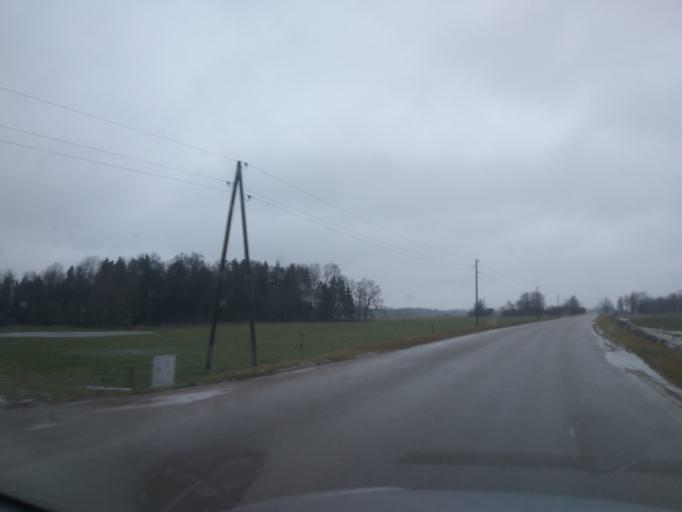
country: LV
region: Saldus Rajons
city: Saldus
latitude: 56.8312
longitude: 22.3757
